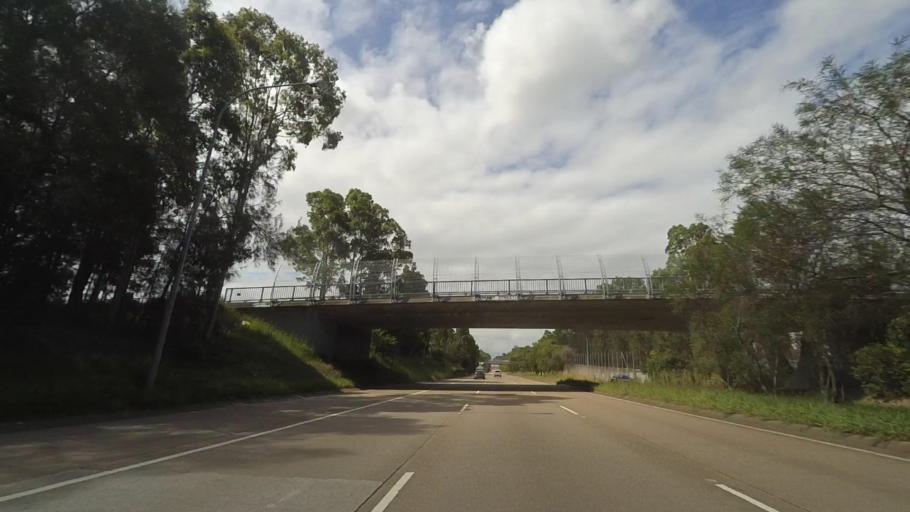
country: AU
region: New South Wales
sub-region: Newcastle
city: North Lambton
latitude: -32.9016
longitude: 151.6937
